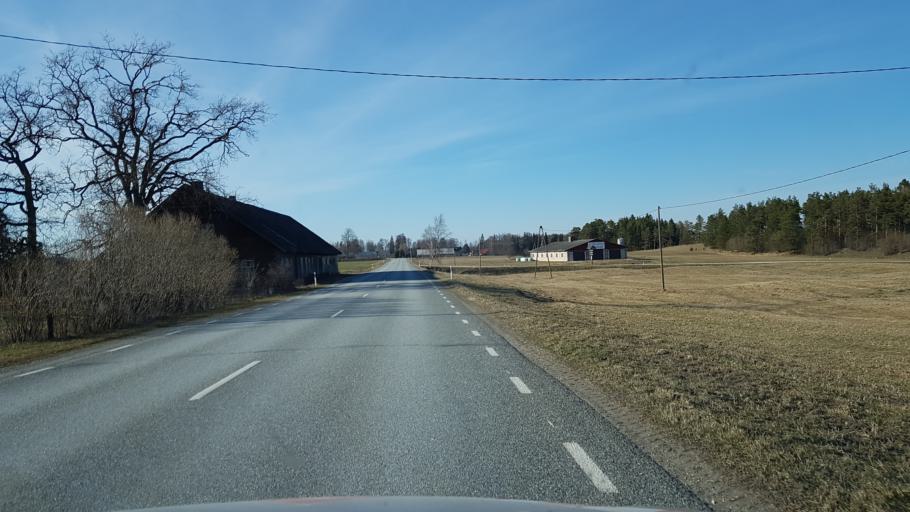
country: EE
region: Laeaene-Virumaa
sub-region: Vinni vald
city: Vinni
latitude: 59.2002
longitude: 26.5612
